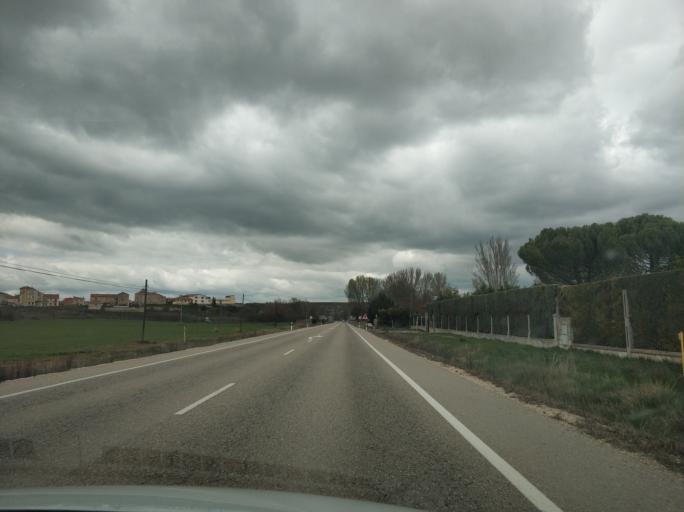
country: ES
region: Castille and Leon
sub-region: Provincia de Burgos
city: Saldana de Burgos
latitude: 42.2568
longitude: -3.6924
